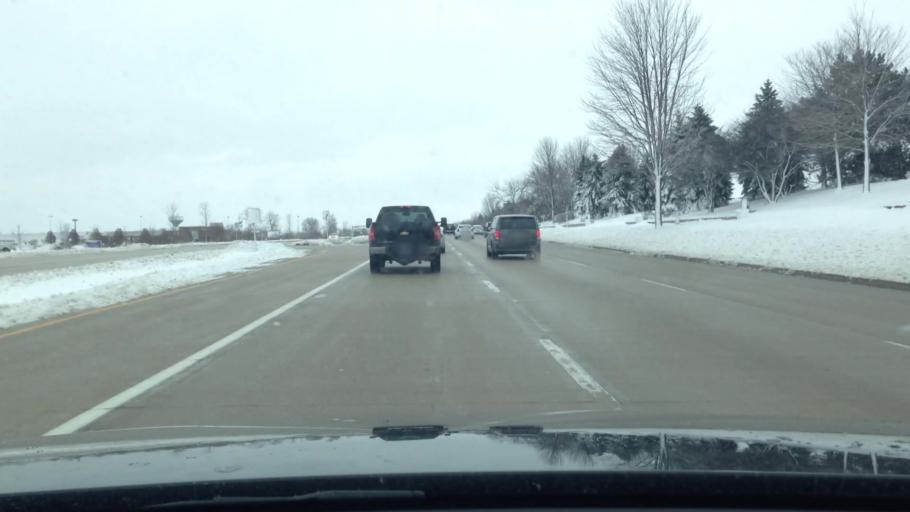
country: US
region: Illinois
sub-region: McHenry County
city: Huntley
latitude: 42.1453
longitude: -88.4323
